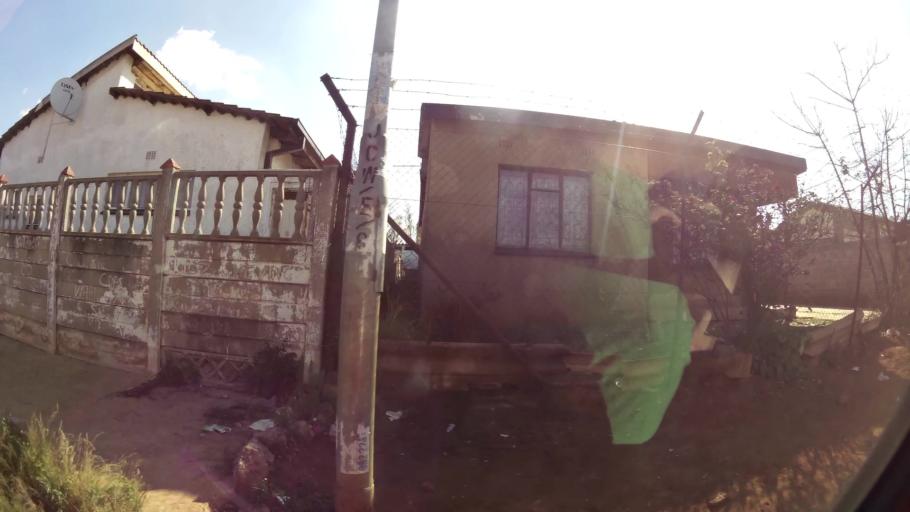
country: ZA
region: Gauteng
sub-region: City of Johannesburg Metropolitan Municipality
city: Soweto
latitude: -26.2354
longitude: 27.8748
